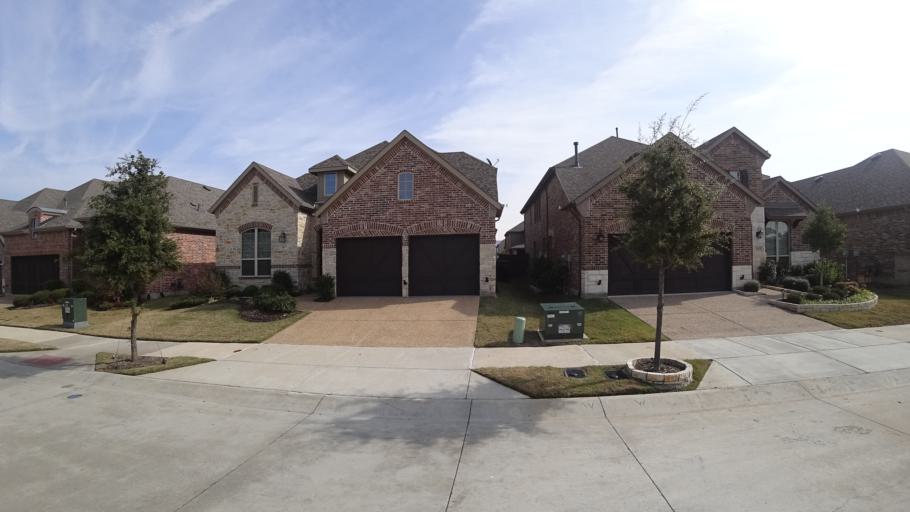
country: US
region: Texas
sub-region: Denton County
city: The Colony
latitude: 33.0647
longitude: -96.8787
